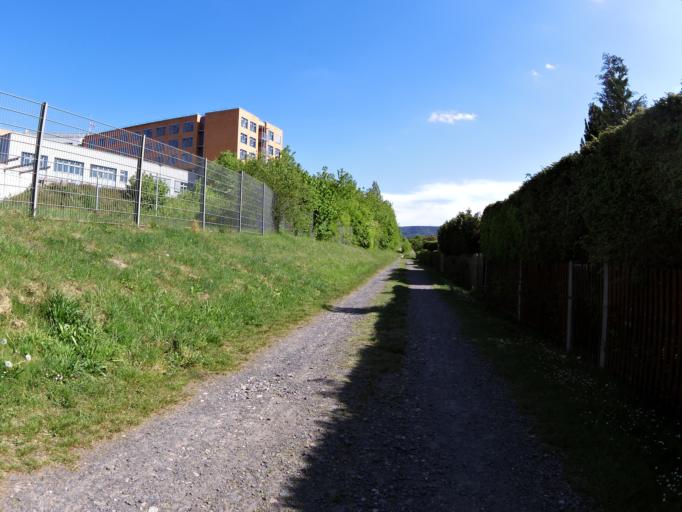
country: DE
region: Thuringia
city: Leimbach
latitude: 50.8043
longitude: 10.2161
